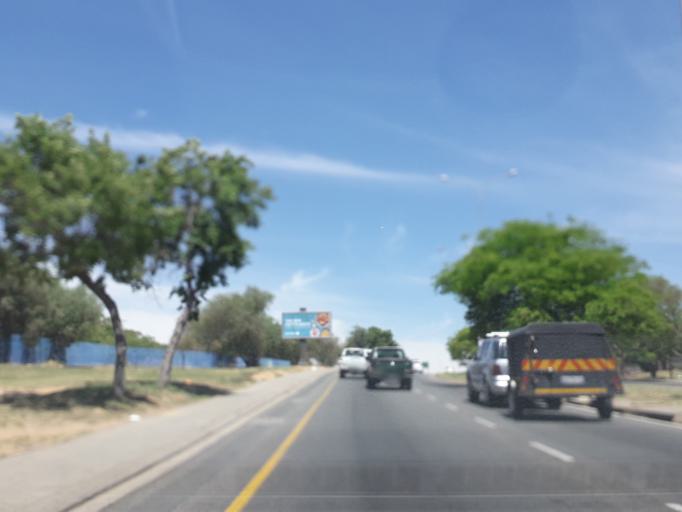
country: ZA
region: Gauteng
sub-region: City of Johannesburg Metropolitan Municipality
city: Modderfontein
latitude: -26.0910
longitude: 28.0894
